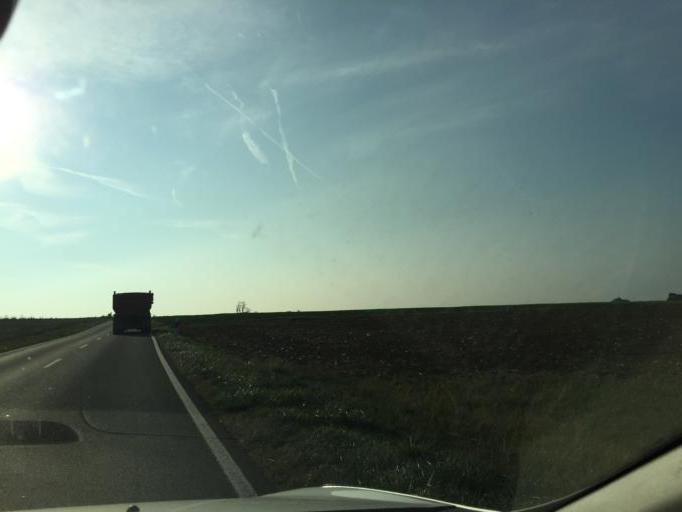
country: LU
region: Grevenmacher
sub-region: Canton de Remich
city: Dalheim
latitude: 49.5429
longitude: 6.2375
